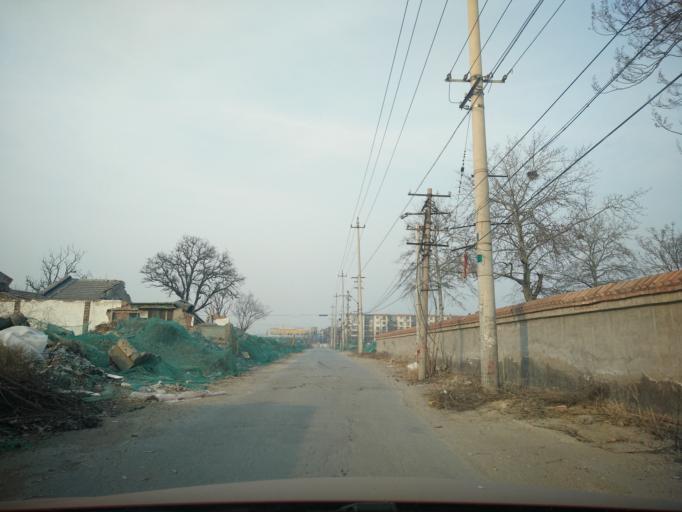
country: CN
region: Beijing
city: Jiugong
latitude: 39.7985
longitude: 116.4250
